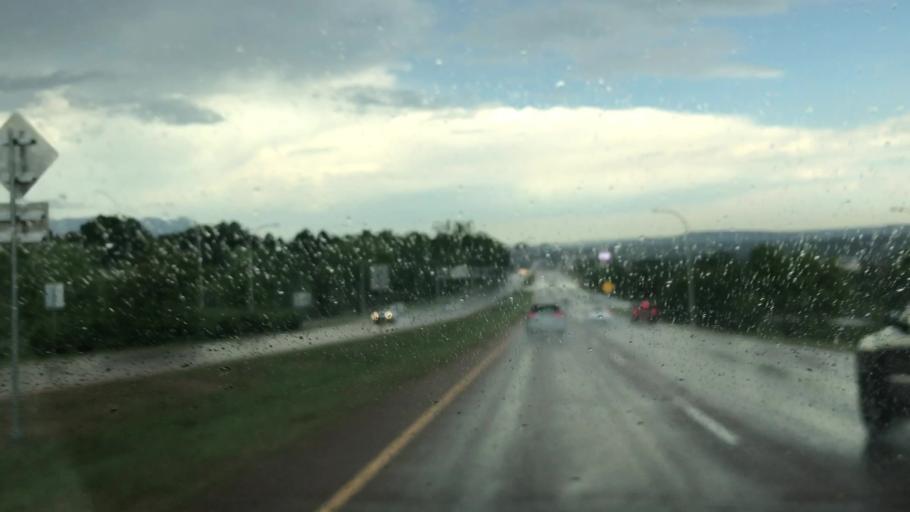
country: US
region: Colorado
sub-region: El Paso County
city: Colorado Springs
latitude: 38.7982
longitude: -104.8221
